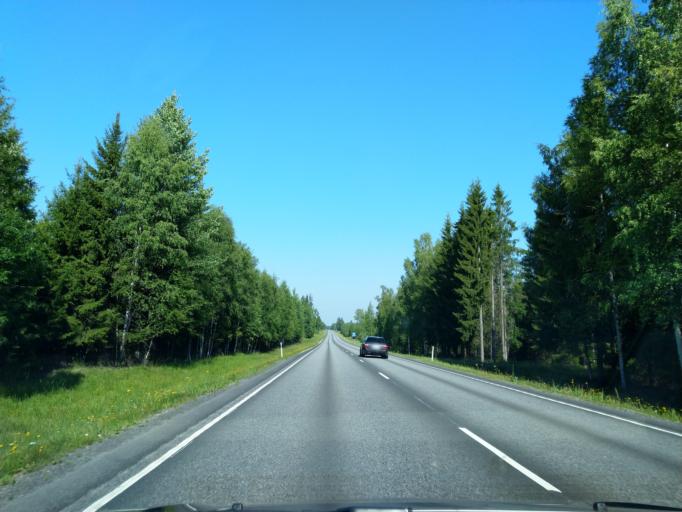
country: FI
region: Satakunta
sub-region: Pori
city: Huittinen
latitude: 61.1300
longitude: 22.7920
